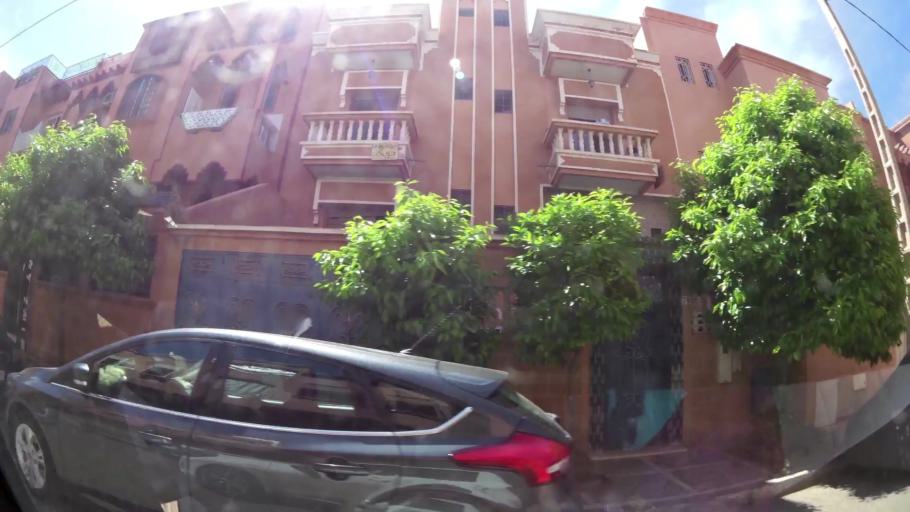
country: MA
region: Marrakech-Tensift-Al Haouz
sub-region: Marrakech
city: Marrakesh
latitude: 31.6615
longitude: -7.9996
